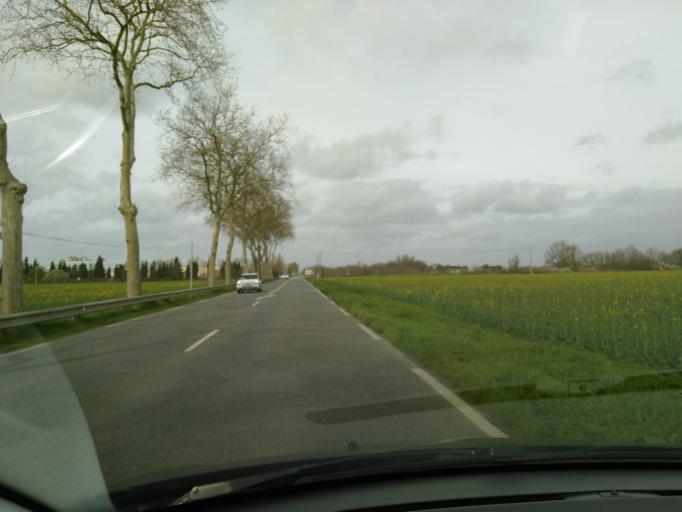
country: FR
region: Midi-Pyrenees
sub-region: Departement de la Haute-Garonne
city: Seilh
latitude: 43.7160
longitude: 1.3341
